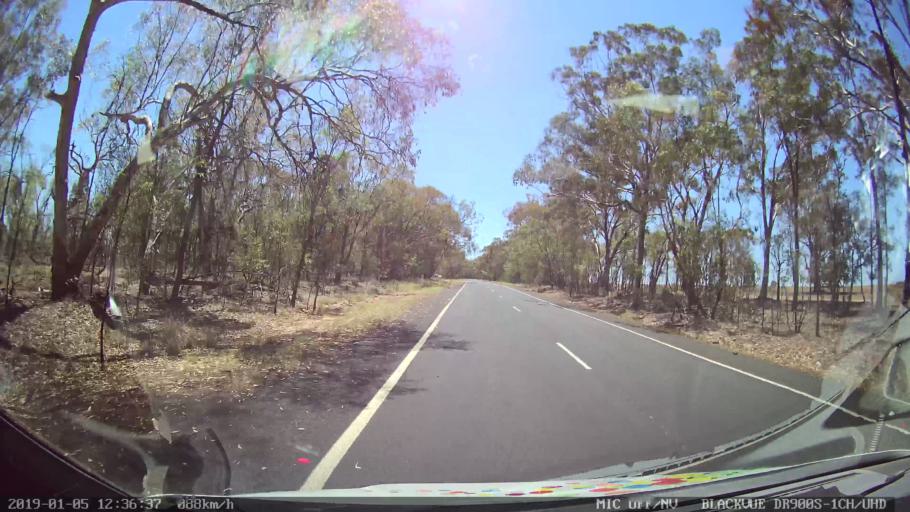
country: AU
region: New South Wales
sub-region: Warrumbungle Shire
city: Coonabarabran
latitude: -31.2067
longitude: 149.4430
